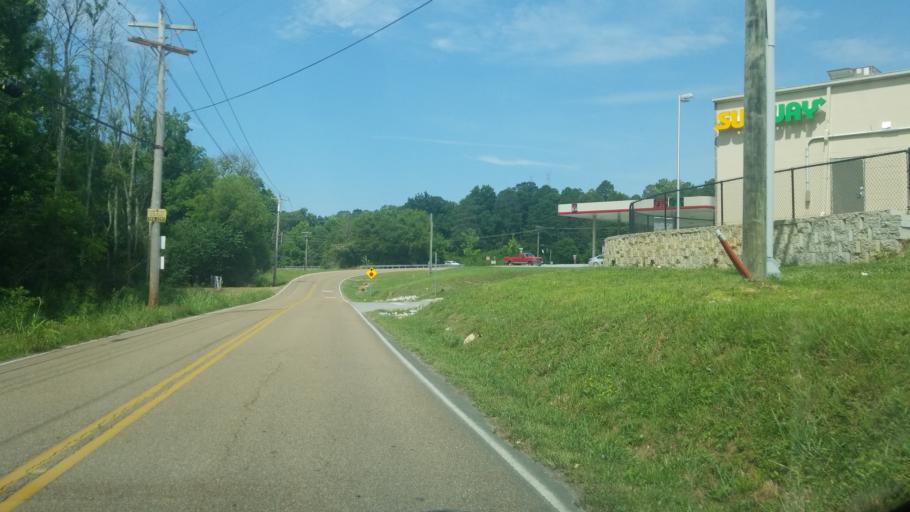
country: US
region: Tennessee
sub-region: Hamilton County
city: Lakesite
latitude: 35.1681
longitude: -85.0761
